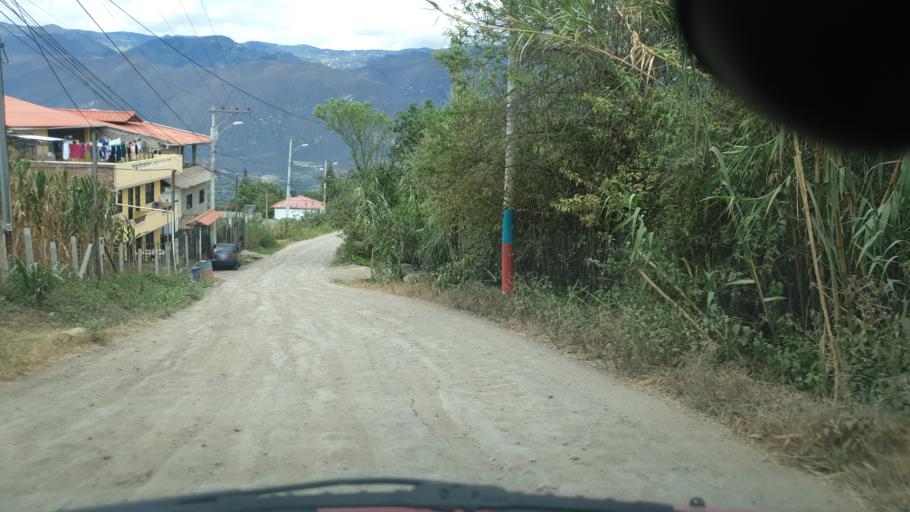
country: EC
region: Azuay
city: Cuenca
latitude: -3.2766
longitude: -79.3107
